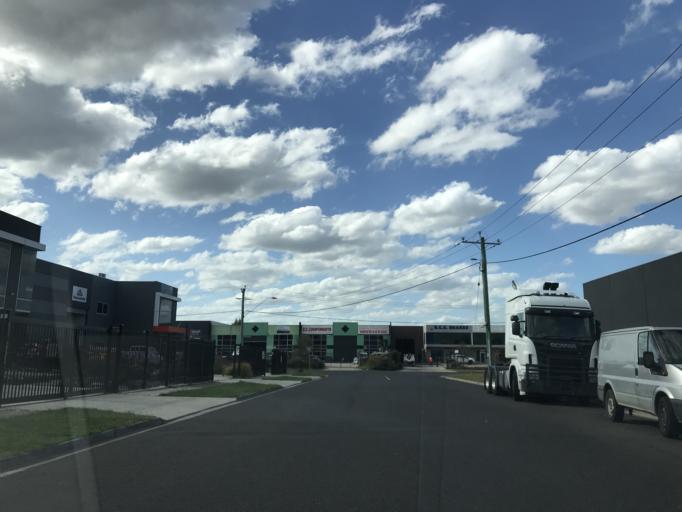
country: AU
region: Victoria
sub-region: Brimbank
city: Sunshine West
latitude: -37.8053
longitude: 144.8153
